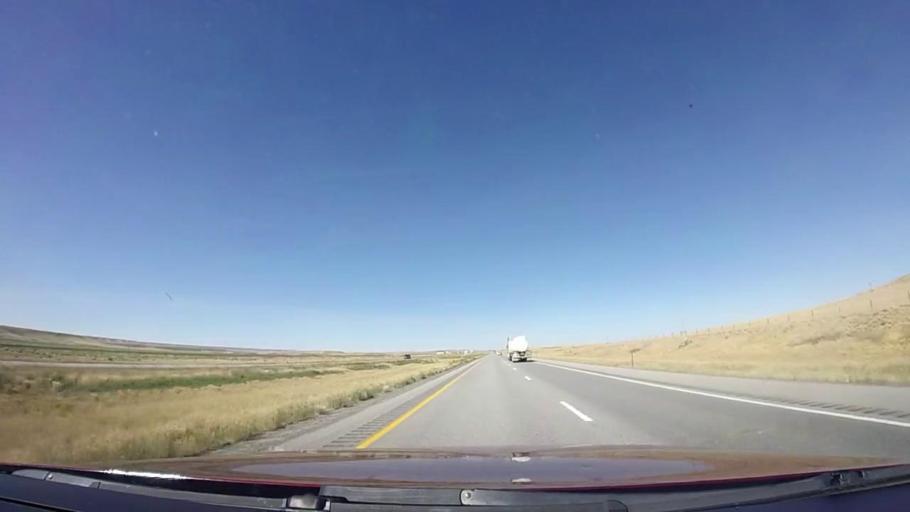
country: US
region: Wyoming
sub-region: Carbon County
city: Rawlins
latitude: 41.6555
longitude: -108.1067
